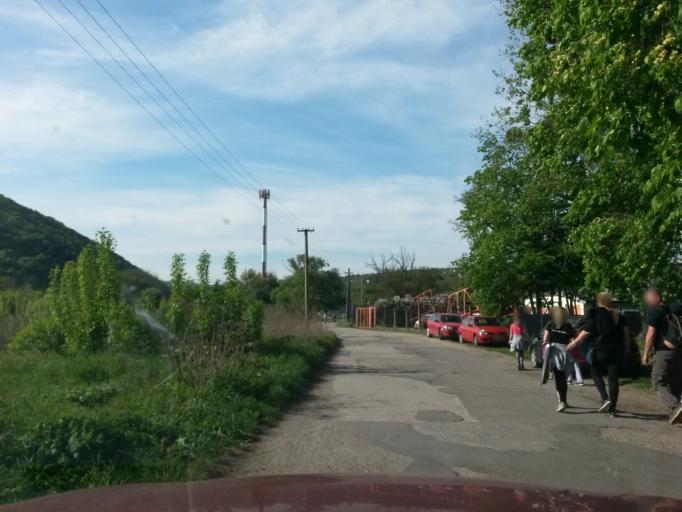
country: SK
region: Kosicky
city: Kosice
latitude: 48.7543
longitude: 21.2523
